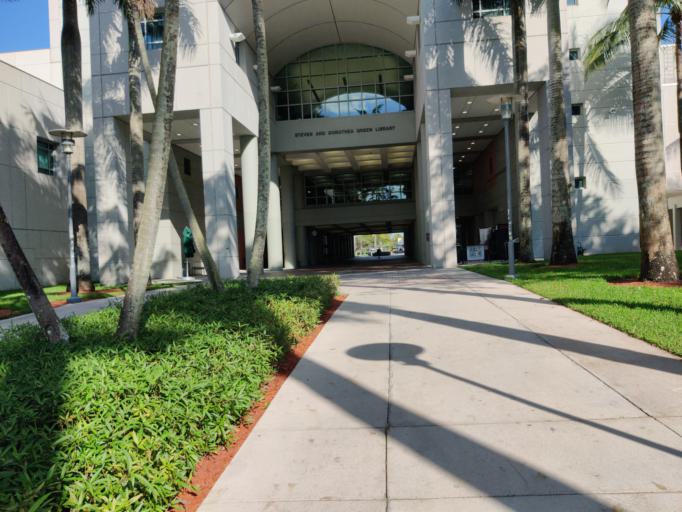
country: US
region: Florida
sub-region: Miami-Dade County
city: Sweetwater
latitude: 25.7569
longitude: -80.3744
